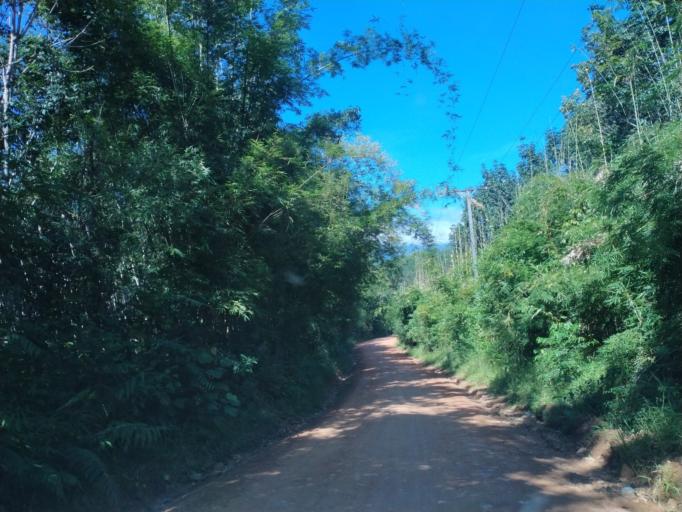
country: TH
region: Changwat Bueng Kan
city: Pak Khat
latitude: 18.6346
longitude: 103.0482
